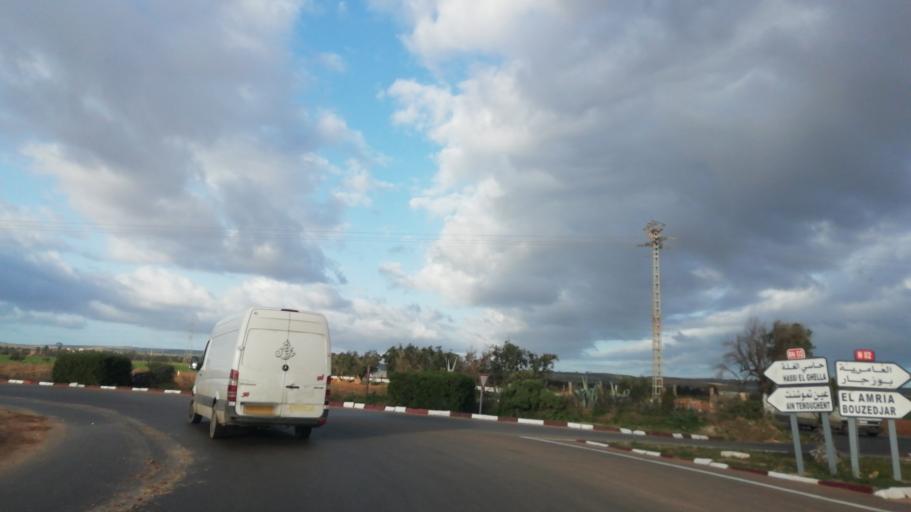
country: DZ
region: Ain Temouchent
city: El Amria
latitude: 35.5147
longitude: -1.0260
